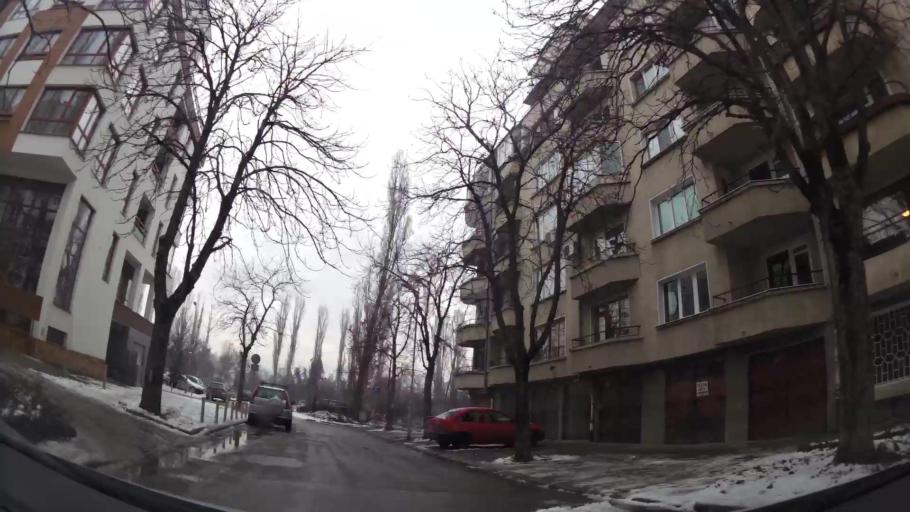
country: BG
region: Sofia-Capital
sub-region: Stolichna Obshtina
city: Sofia
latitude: 42.6879
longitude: 23.2944
